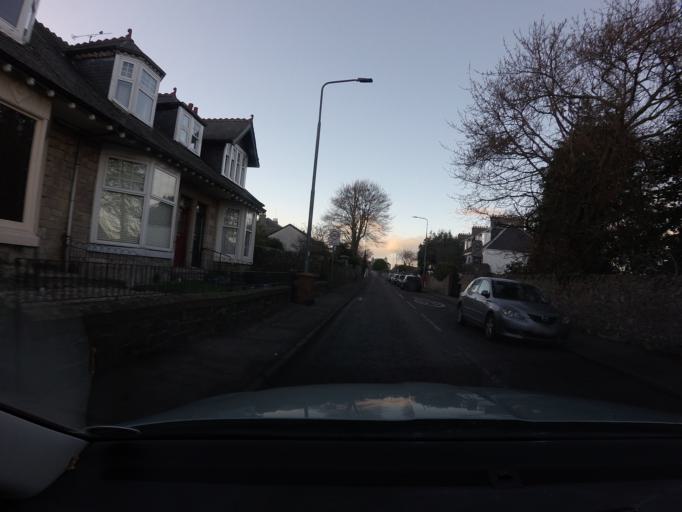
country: GB
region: Scotland
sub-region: Fife
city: Tayport
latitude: 56.4507
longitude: -2.8838
